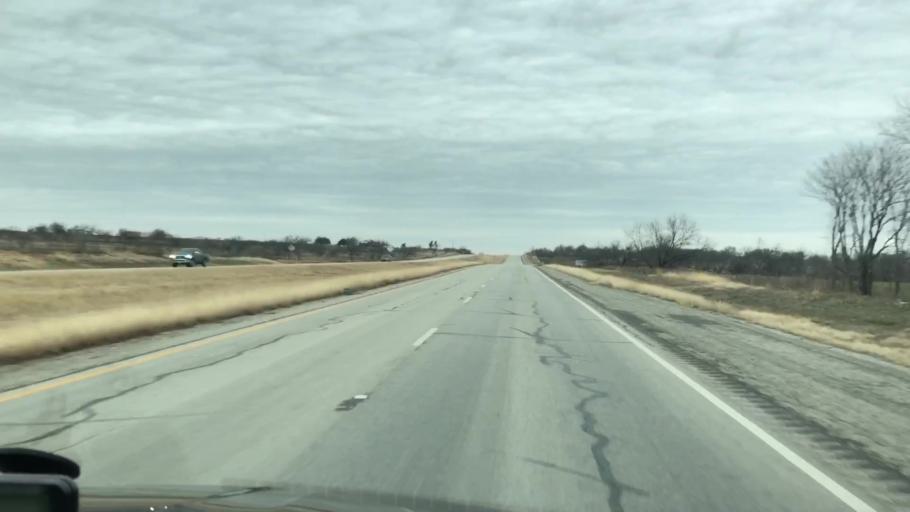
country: US
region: Texas
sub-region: Jack County
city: Jacksboro
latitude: 33.2411
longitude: -98.2195
